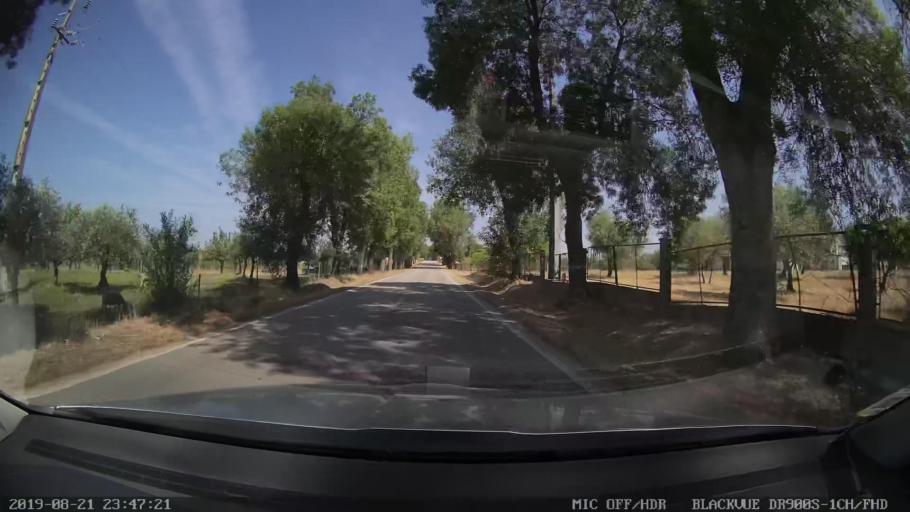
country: PT
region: Castelo Branco
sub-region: Idanha-A-Nova
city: Idanha-a-Nova
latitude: 39.8509
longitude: -7.2573
